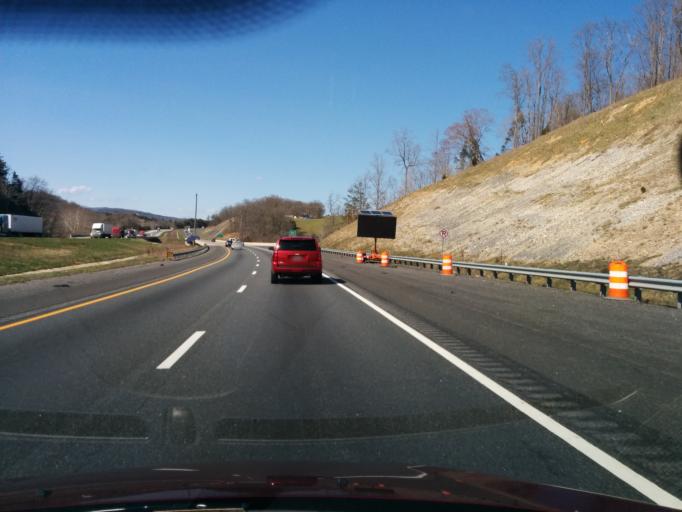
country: US
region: Virginia
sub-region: Rockbridge County
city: East Lexington
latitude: 37.7754
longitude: -79.4008
